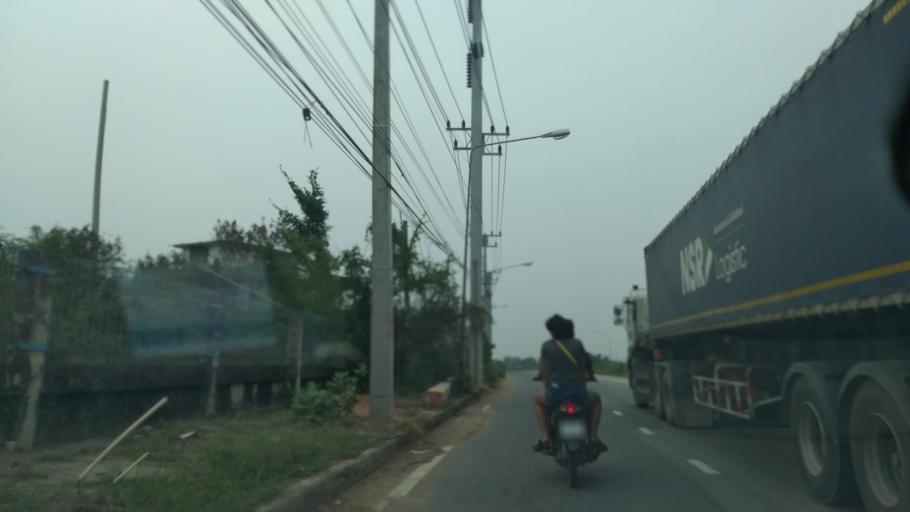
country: TH
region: Chon Buri
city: Ko Chan
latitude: 13.4751
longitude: 101.2837
